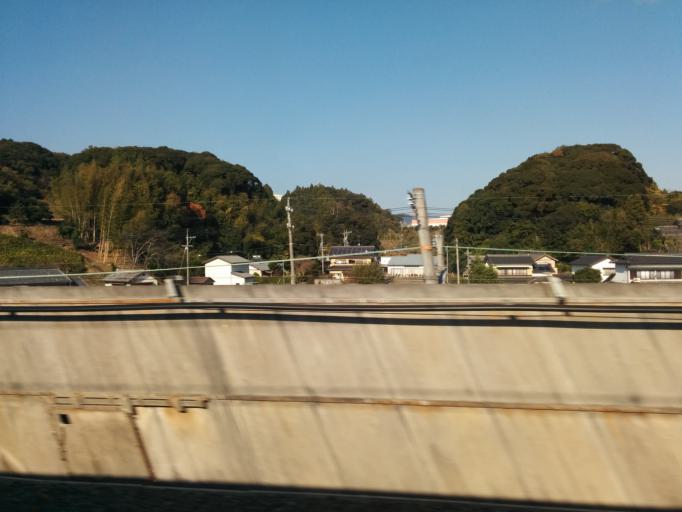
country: JP
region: Shizuoka
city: Kakegawa
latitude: 34.7727
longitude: 138.0487
